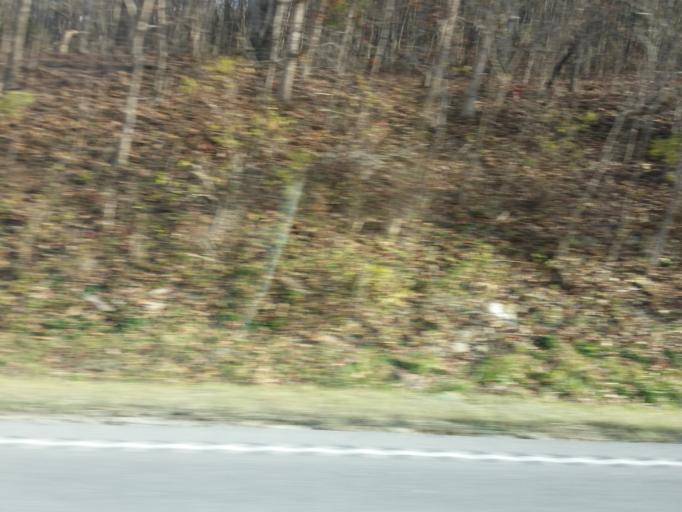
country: US
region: Kentucky
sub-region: Pendleton County
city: Falmouth
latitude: 38.7395
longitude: -84.3684
